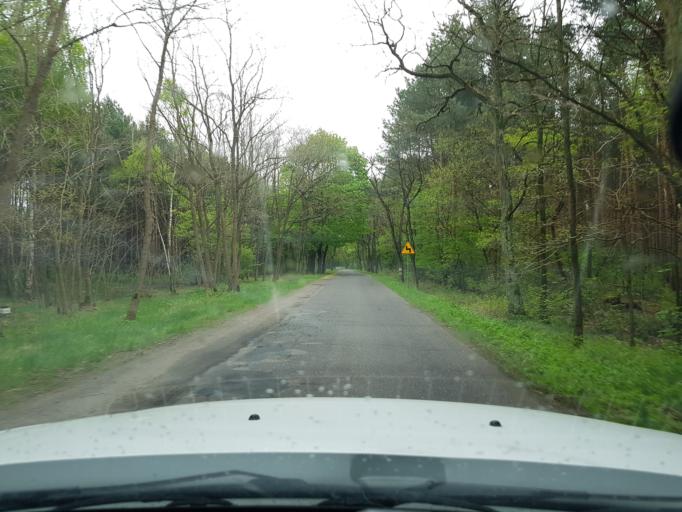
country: PL
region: West Pomeranian Voivodeship
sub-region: Powiat mysliborski
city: Debno
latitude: 52.7004
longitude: 14.6620
